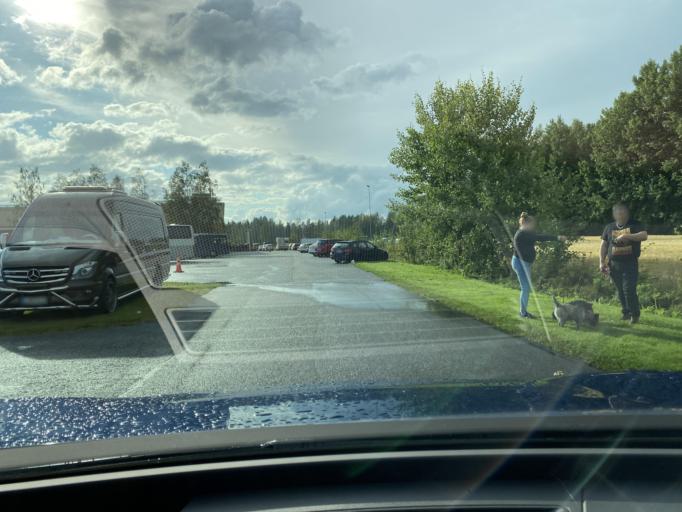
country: FI
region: Southern Ostrobothnia
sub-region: Seinaejoki
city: Alahaermae
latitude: 63.2307
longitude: 22.8470
